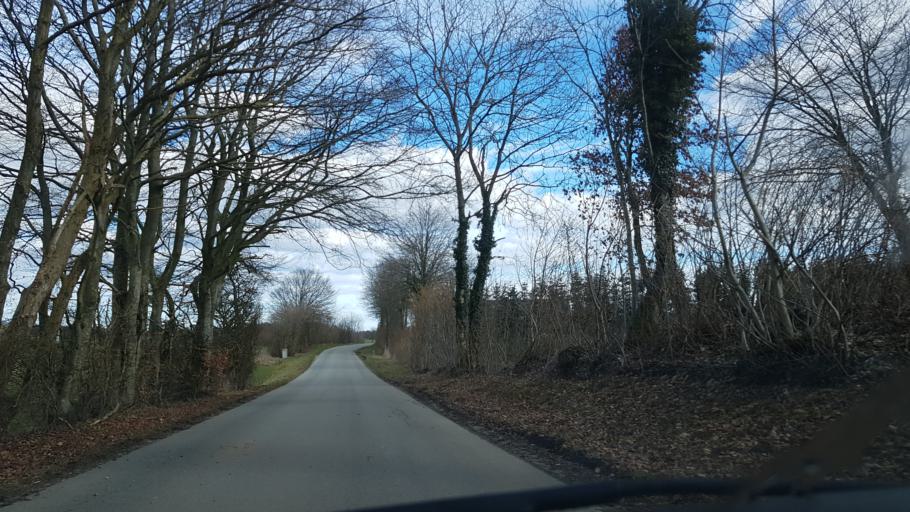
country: DK
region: South Denmark
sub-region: Kolding Kommune
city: Christiansfeld
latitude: 55.3534
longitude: 9.4161
